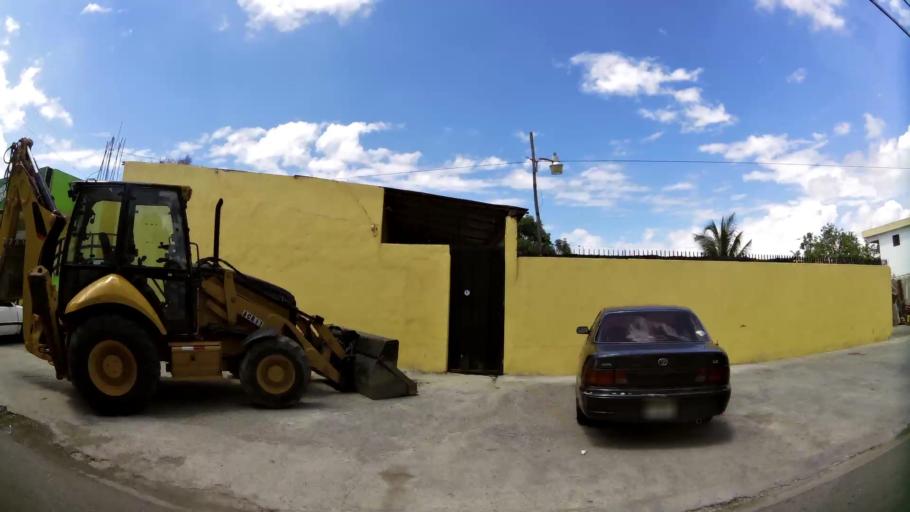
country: DO
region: Santiago
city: Santiago de los Caballeros
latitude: 19.4592
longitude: -70.6671
